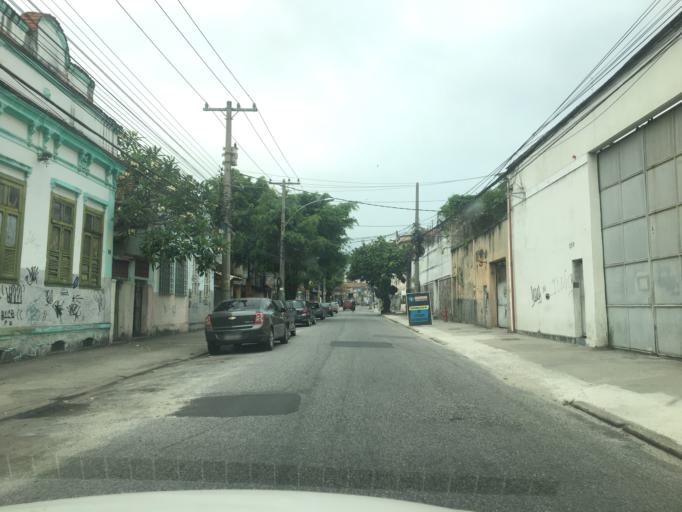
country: BR
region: Rio de Janeiro
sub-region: Rio De Janeiro
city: Rio de Janeiro
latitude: -22.8931
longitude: -43.2287
